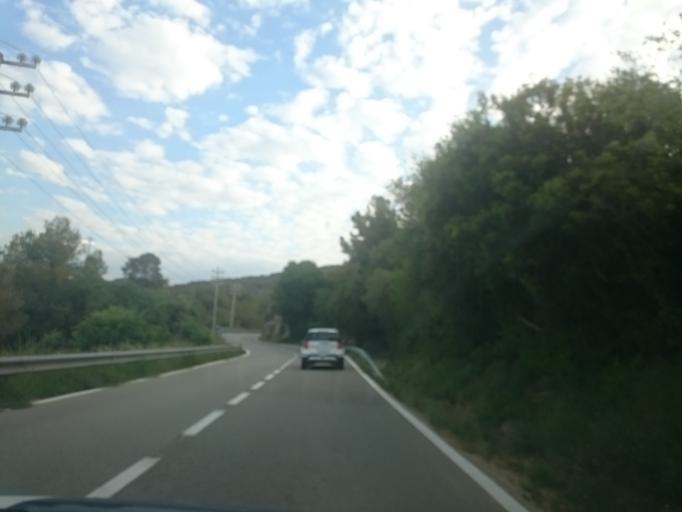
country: ES
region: Catalonia
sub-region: Provincia de Barcelona
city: Cubelles
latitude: 41.2362
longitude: 1.6638
